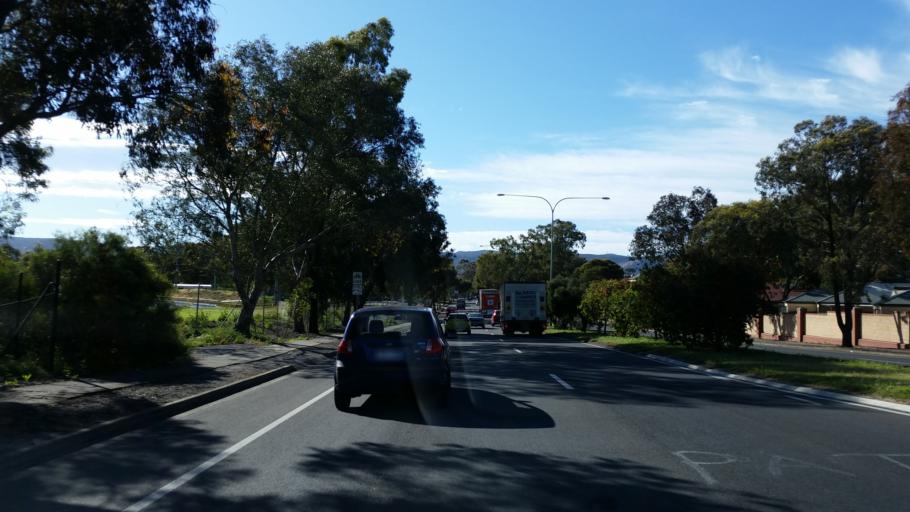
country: AU
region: South Australia
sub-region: Norwood Payneham St Peters
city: Marden
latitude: -34.8909
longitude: 138.6317
